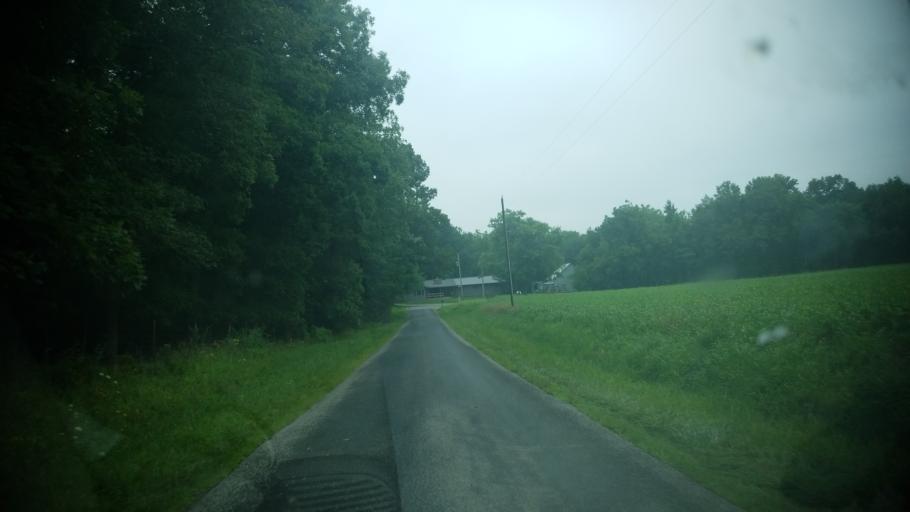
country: US
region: Illinois
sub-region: Clay County
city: Flora
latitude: 38.5748
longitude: -88.3648
